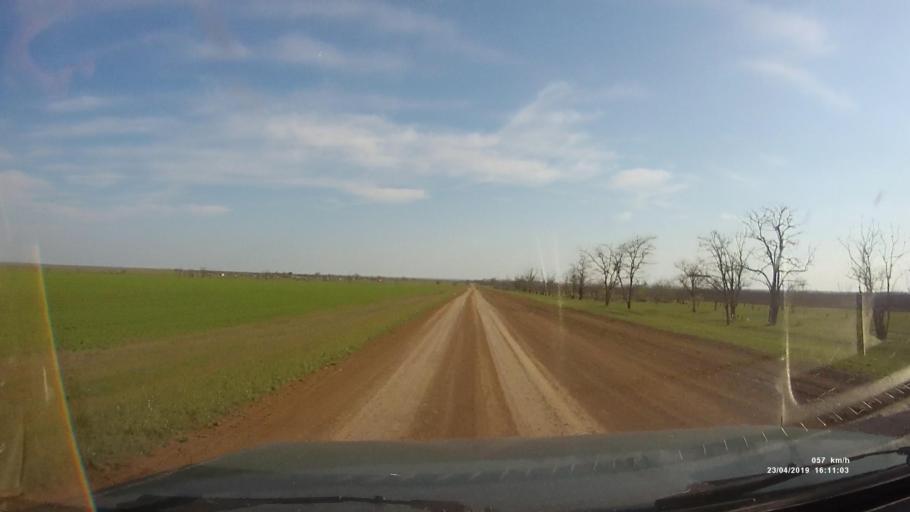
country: RU
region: Rostov
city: Remontnoye
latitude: 46.4772
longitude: 43.1231
